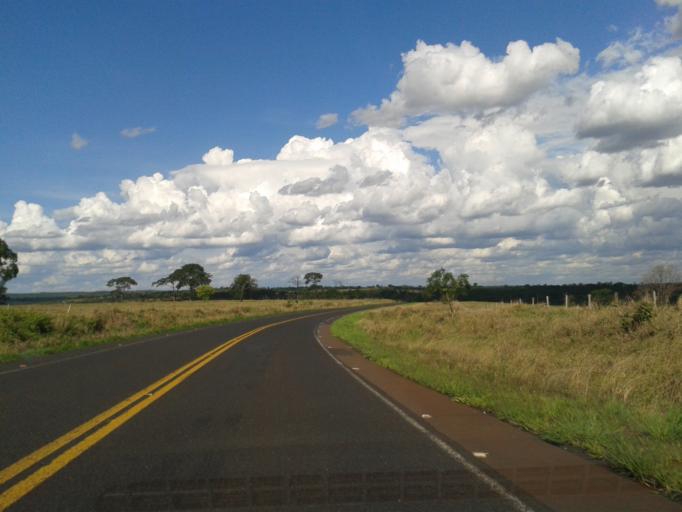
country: BR
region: Minas Gerais
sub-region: Campina Verde
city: Campina Verde
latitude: -19.5557
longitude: -49.8173
